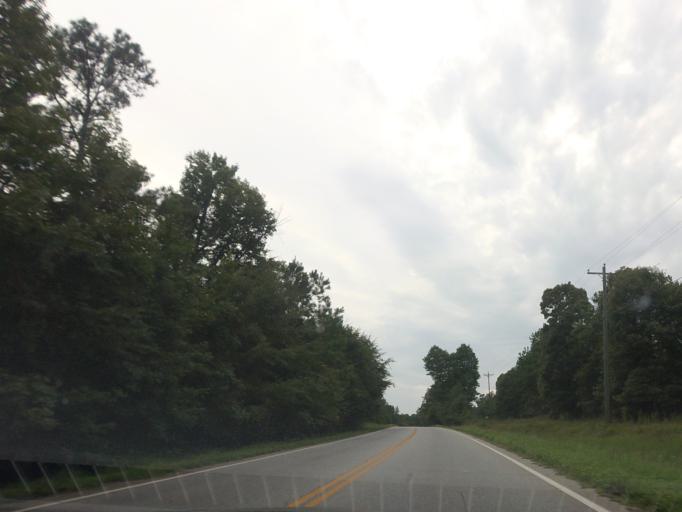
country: US
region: Georgia
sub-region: Twiggs County
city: Jeffersonville
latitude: 32.7640
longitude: -83.4651
